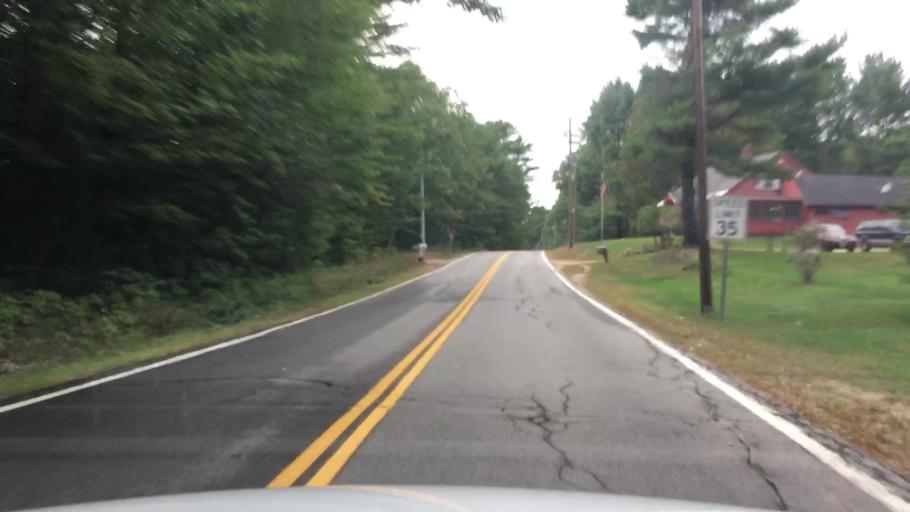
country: US
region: New Hampshire
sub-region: Carroll County
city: Effingham
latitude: 43.7129
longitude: -70.9840
